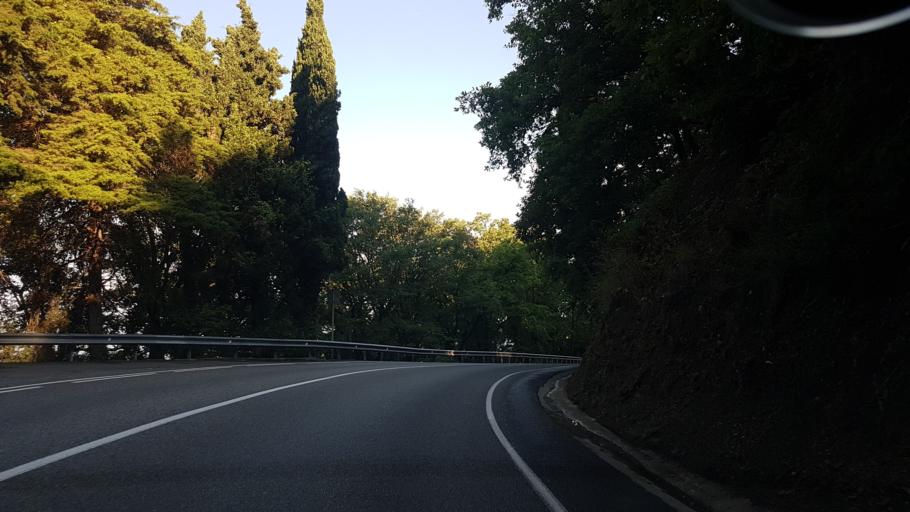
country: RU
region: Krasnodarskiy
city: Vardane
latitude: 43.8069
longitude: 39.4495
